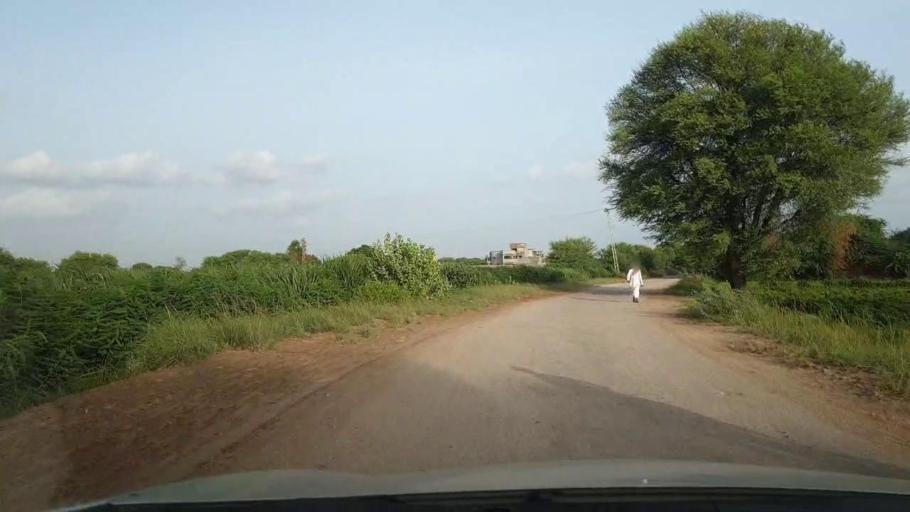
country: PK
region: Sindh
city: Tando Ghulam Ali
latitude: 25.0975
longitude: 68.8880
